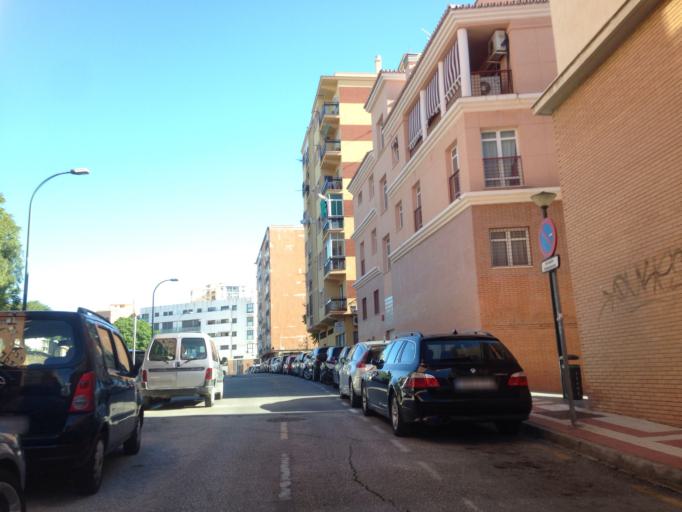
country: ES
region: Andalusia
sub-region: Provincia de Malaga
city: Malaga
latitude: 36.7270
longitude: -4.4154
